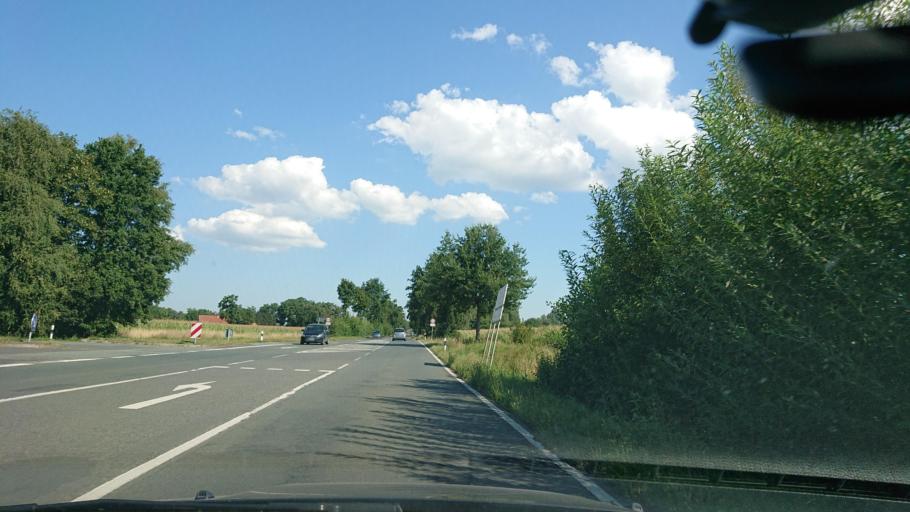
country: DE
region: North Rhine-Westphalia
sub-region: Regierungsbezirk Detmold
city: Delbruck
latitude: 51.7996
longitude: 8.5599
